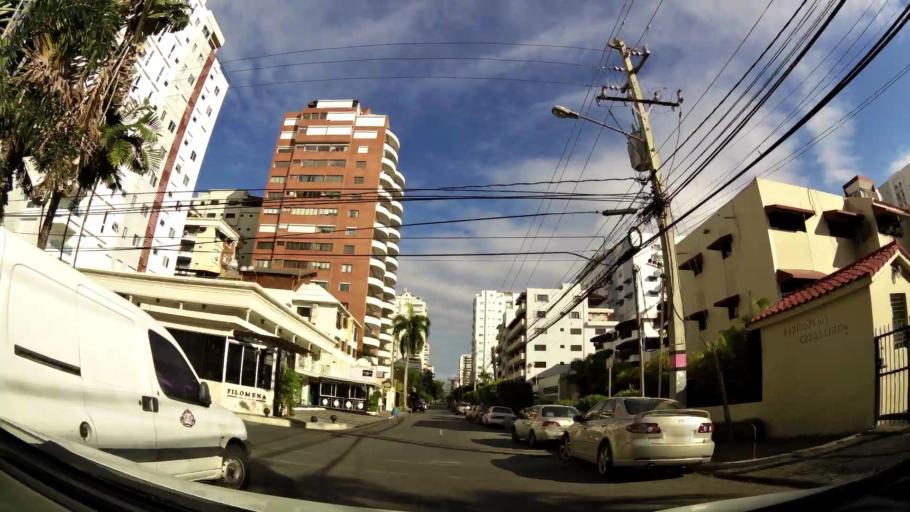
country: DO
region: Nacional
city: La Julia
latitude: 18.4766
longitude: -69.9390
